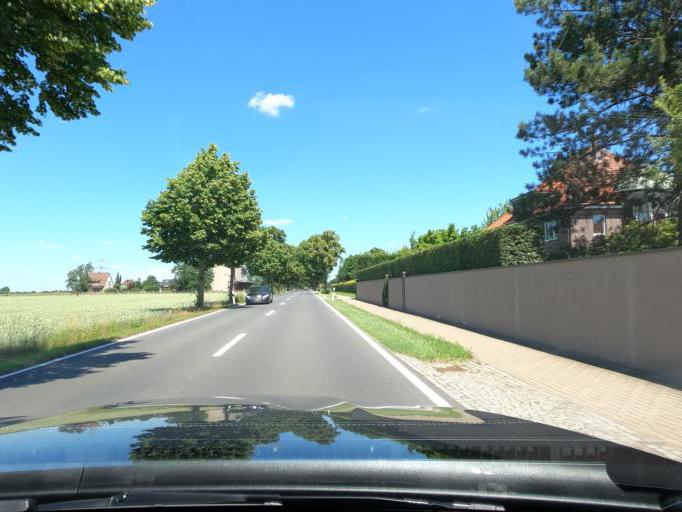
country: DE
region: Lower Saxony
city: Lehrte
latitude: 52.4076
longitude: 9.9744
